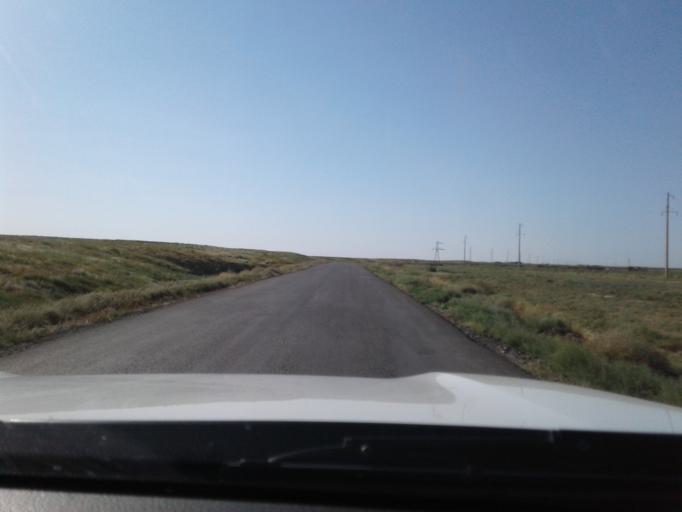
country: IR
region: Razavi Khorasan
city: Kalat-e Naderi
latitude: 37.1568
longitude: 60.0537
